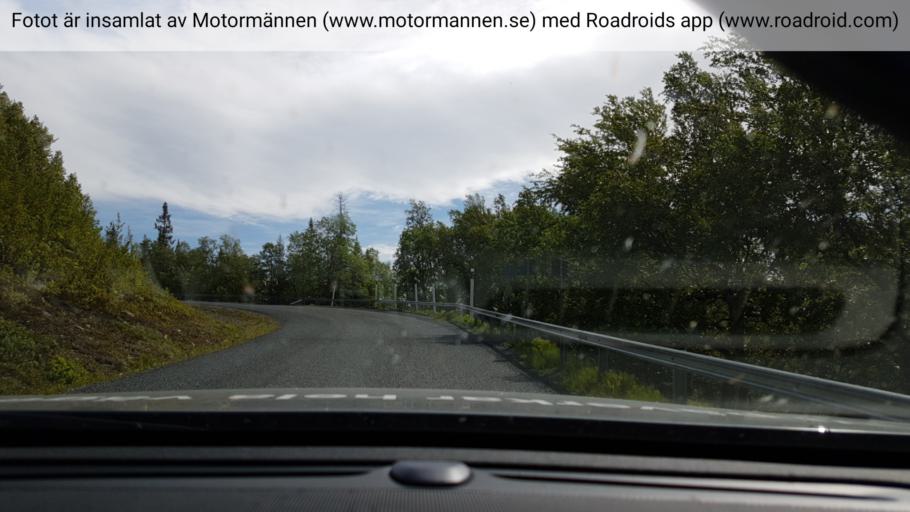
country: SE
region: Vaesterbotten
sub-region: Vilhelmina Kommun
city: Sjoberg
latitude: 65.2376
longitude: 15.4547
